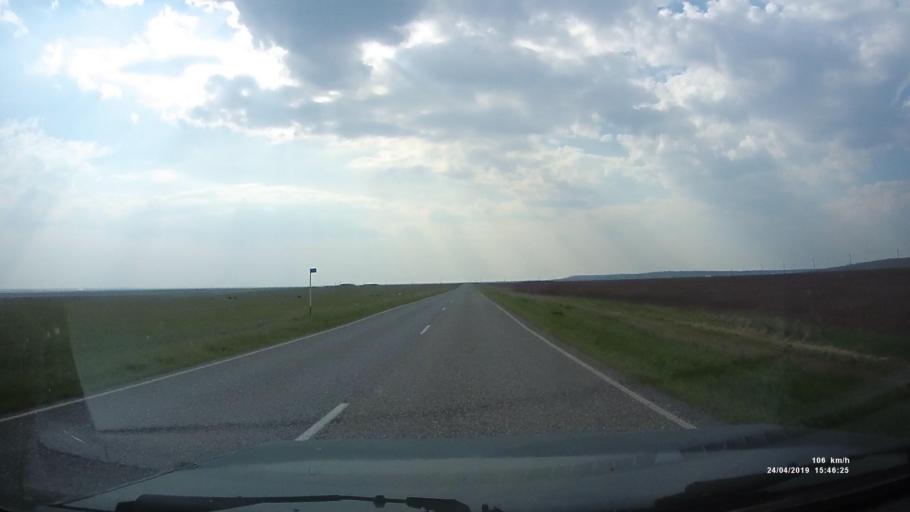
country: RU
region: Kalmykiya
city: Yashalta
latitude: 46.5929
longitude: 42.7150
